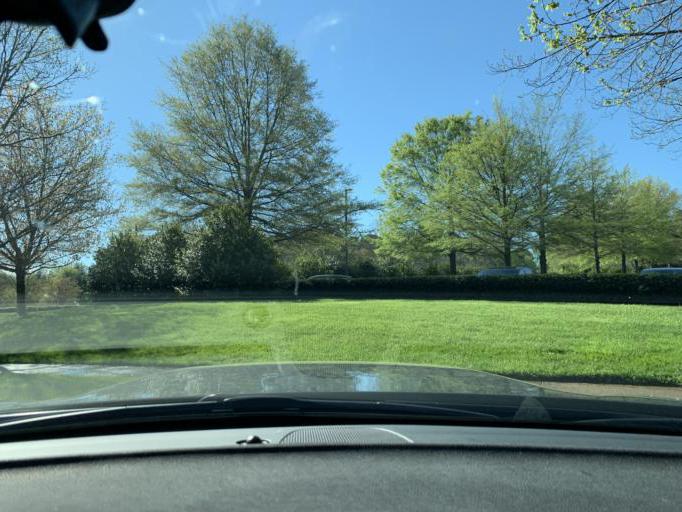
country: US
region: Georgia
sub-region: Fulton County
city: Alpharetta
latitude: 34.0908
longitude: -84.2530
